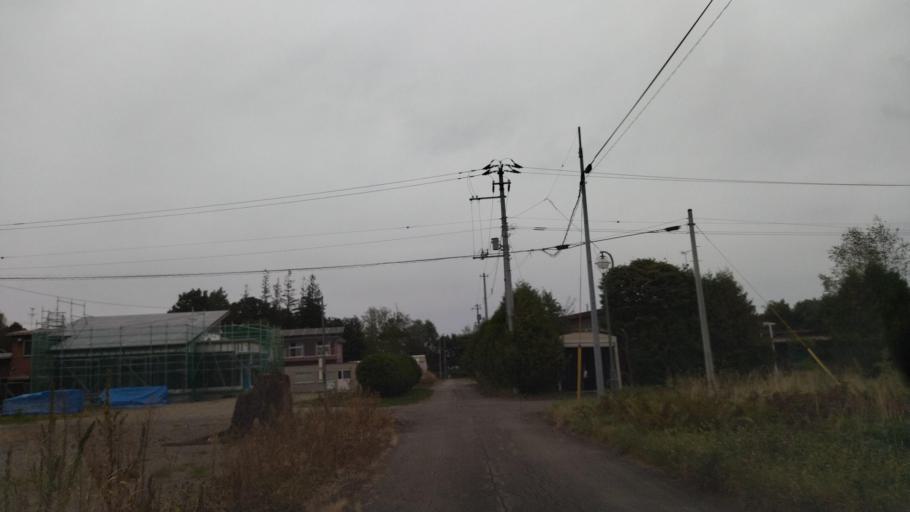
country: JP
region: Hokkaido
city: Otofuke
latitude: 43.2270
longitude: 143.2806
